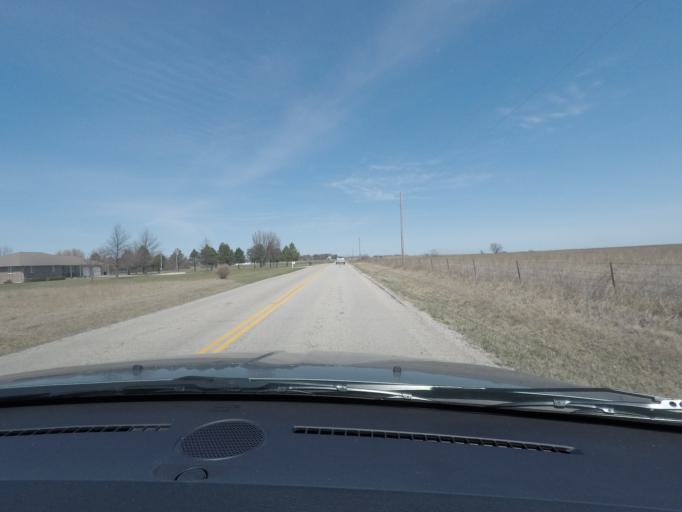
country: US
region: Kansas
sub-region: Lyon County
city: Emporia
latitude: 38.5331
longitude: -96.1700
